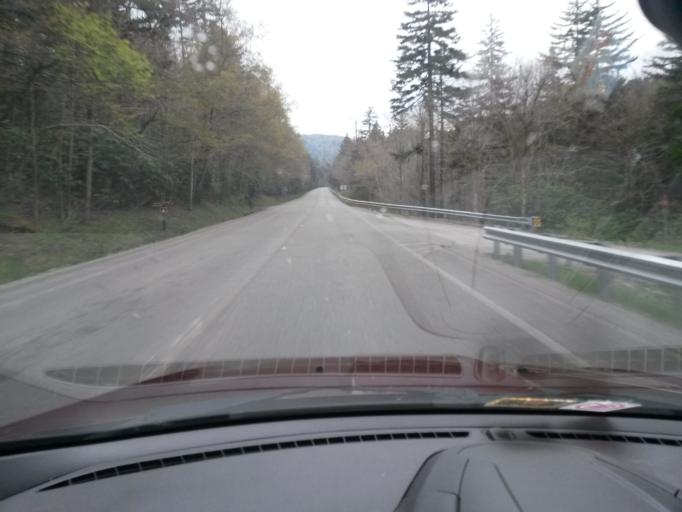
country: US
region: West Virginia
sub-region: Randolph County
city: Elkins
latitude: 38.6284
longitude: -79.8828
